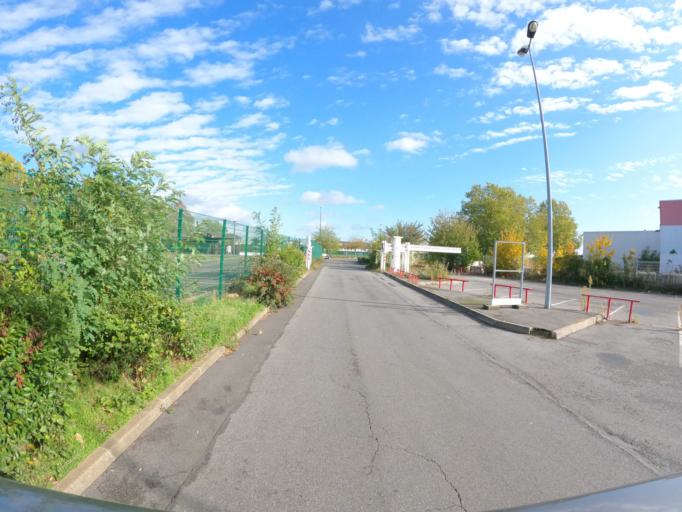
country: FR
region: Ile-de-France
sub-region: Departement de Seine-et-Marne
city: Chelles
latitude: 48.8794
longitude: 2.6120
